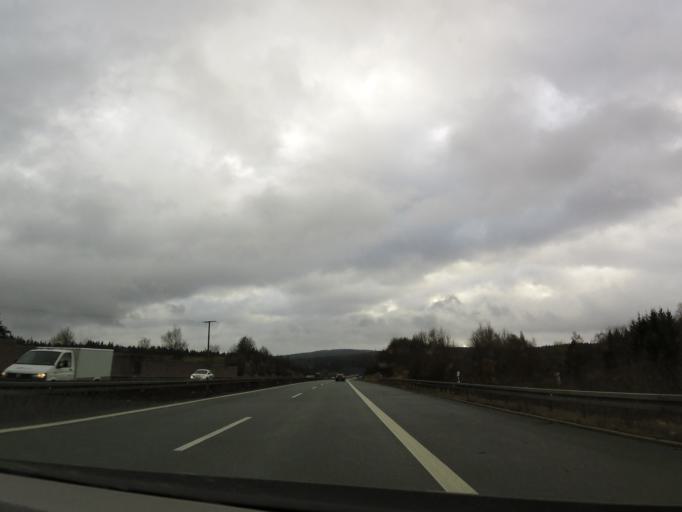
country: DE
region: Bavaria
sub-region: Upper Franconia
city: Rehau
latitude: 50.2428
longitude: 12.0622
